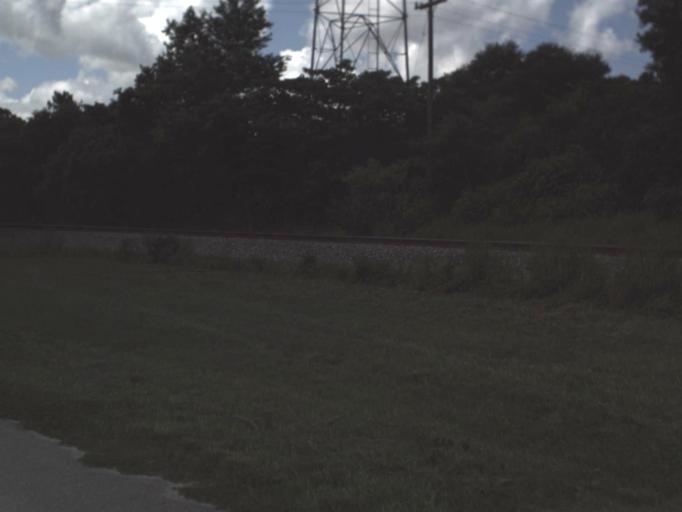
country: US
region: Florida
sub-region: Putnam County
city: Crescent City
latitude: 29.3646
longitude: -81.5081
